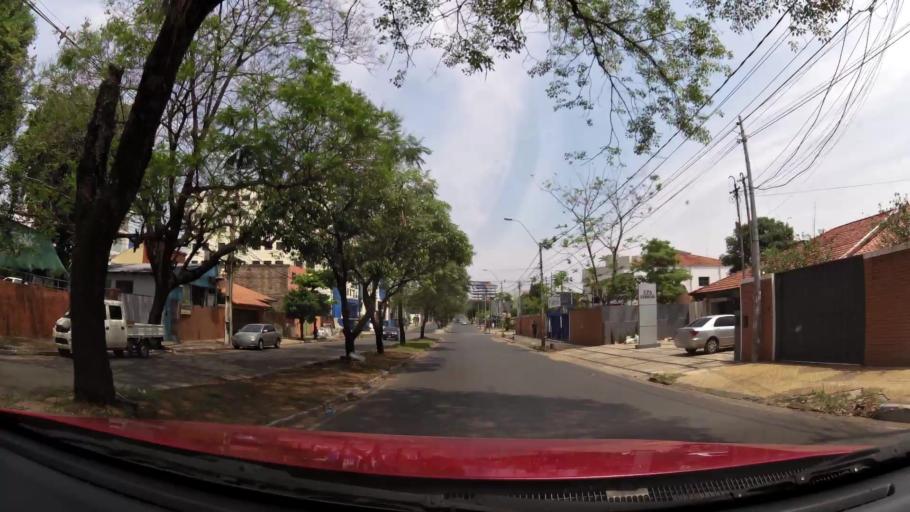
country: PY
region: Asuncion
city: Asuncion
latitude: -25.2773
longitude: -57.5996
